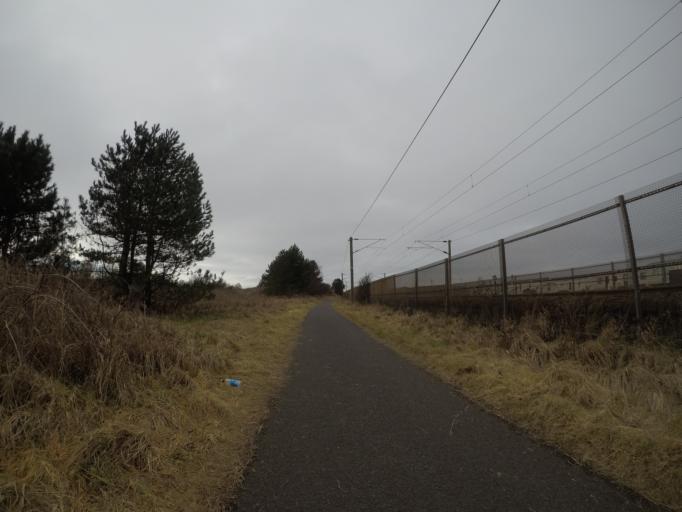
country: GB
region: Scotland
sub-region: North Ayrshire
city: Stevenston
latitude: 55.6325
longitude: -4.7586
